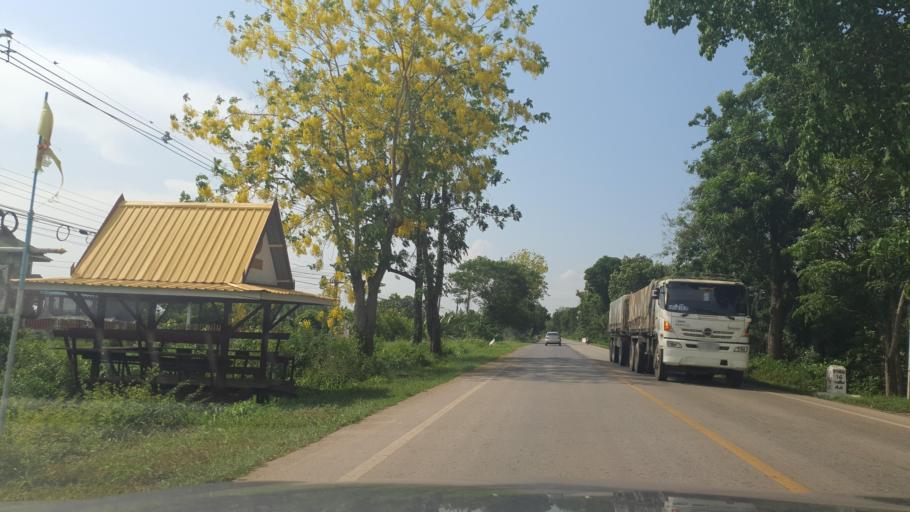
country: TH
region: Sukhothai
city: Si Samrong
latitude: 17.1850
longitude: 99.8518
